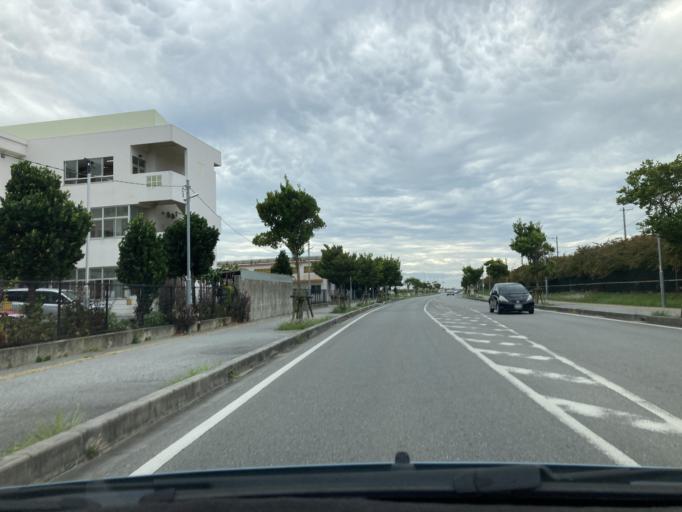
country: JP
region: Okinawa
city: Ishikawa
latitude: 26.3962
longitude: 127.7410
